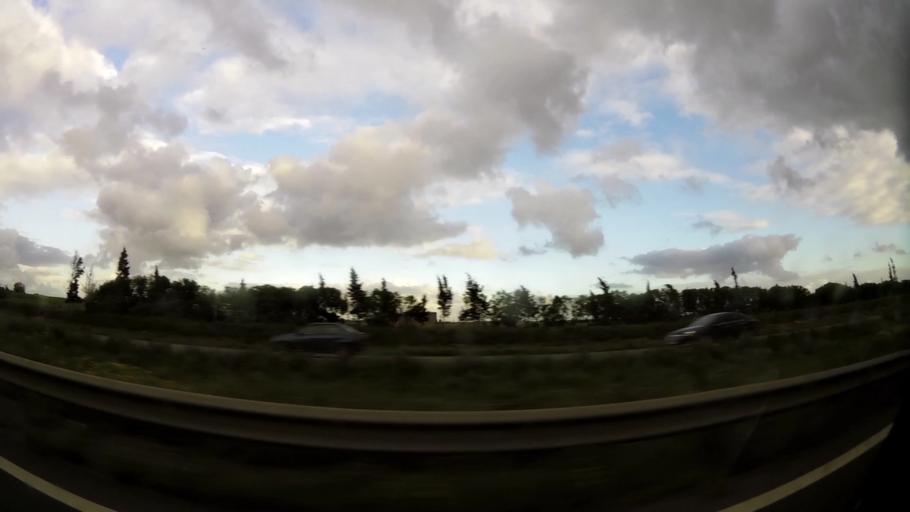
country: MA
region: Grand Casablanca
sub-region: Mediouna
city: Tit Mellil
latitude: 33.5994
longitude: -7.4398
